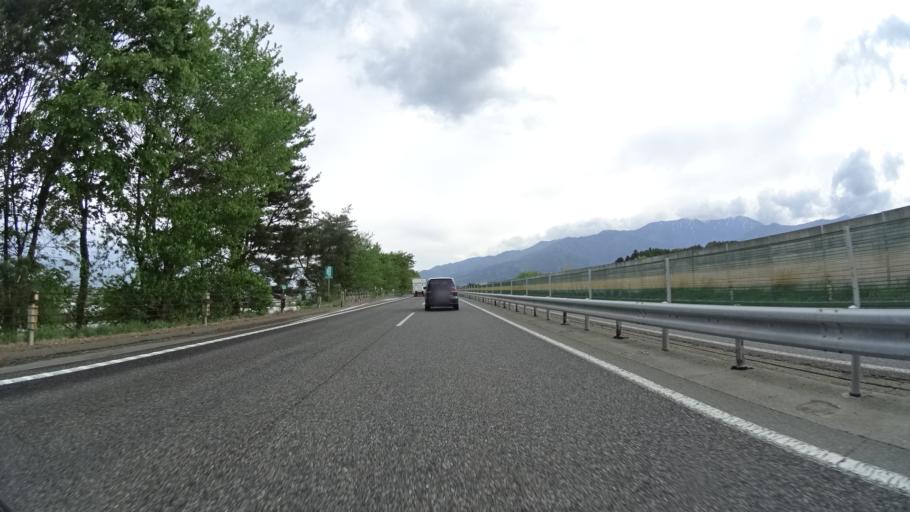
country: JP
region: Nagano
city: Ina
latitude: 35.8745
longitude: 137.9477
